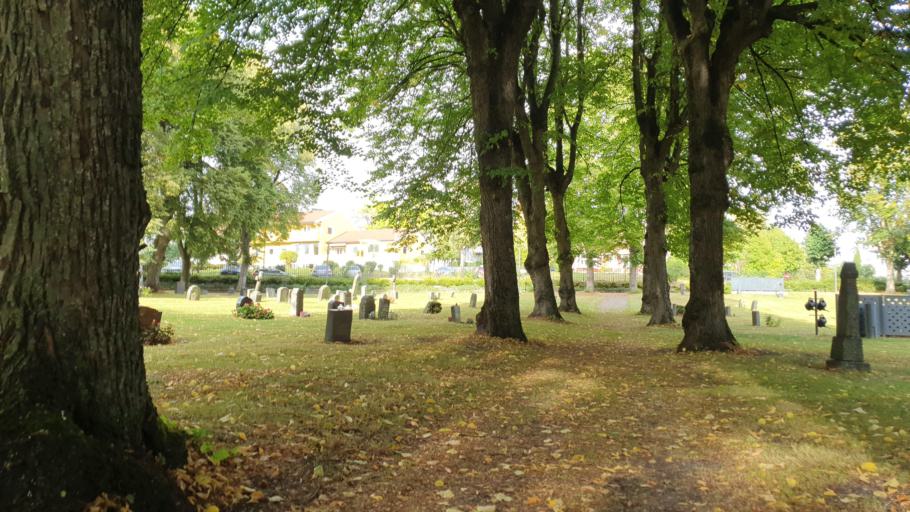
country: NO
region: Vestfold
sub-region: Tonsberg
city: Tonsberg
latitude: 59.2702
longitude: 10.4142
